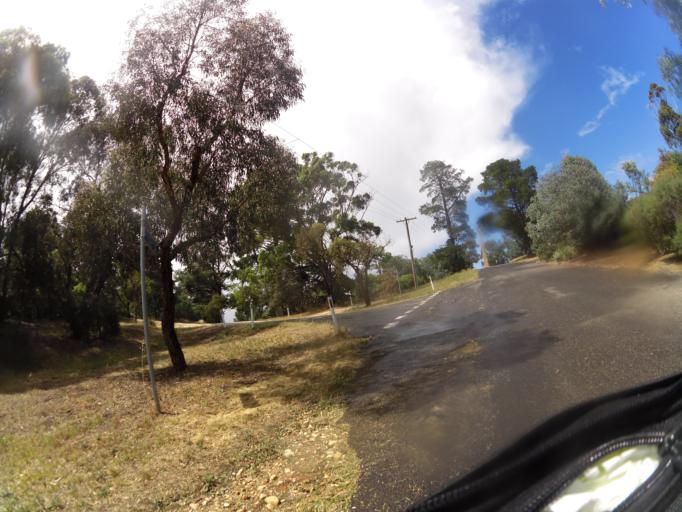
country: AU
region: Victoria
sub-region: Mount Alexander
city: Castlemaine
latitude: -37.0658
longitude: 144.2264
